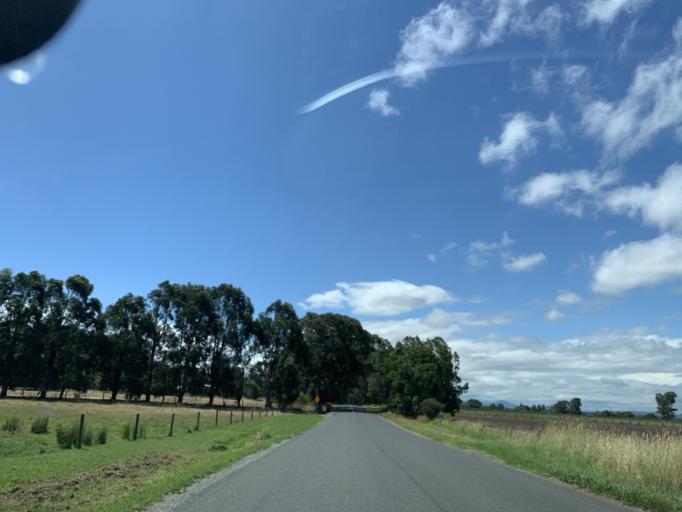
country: AU
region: Victoria
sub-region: Wellington
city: Heyfield
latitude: -38.0072
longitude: 146.6536
